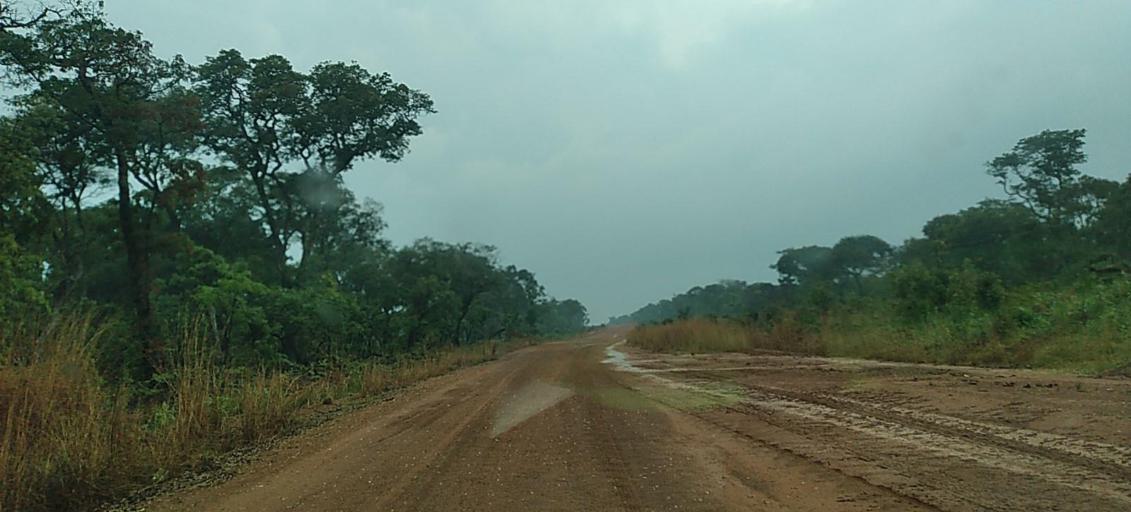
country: ZM
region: North-Western
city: Mwinilunga
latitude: -11.5994
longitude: 24.3929
